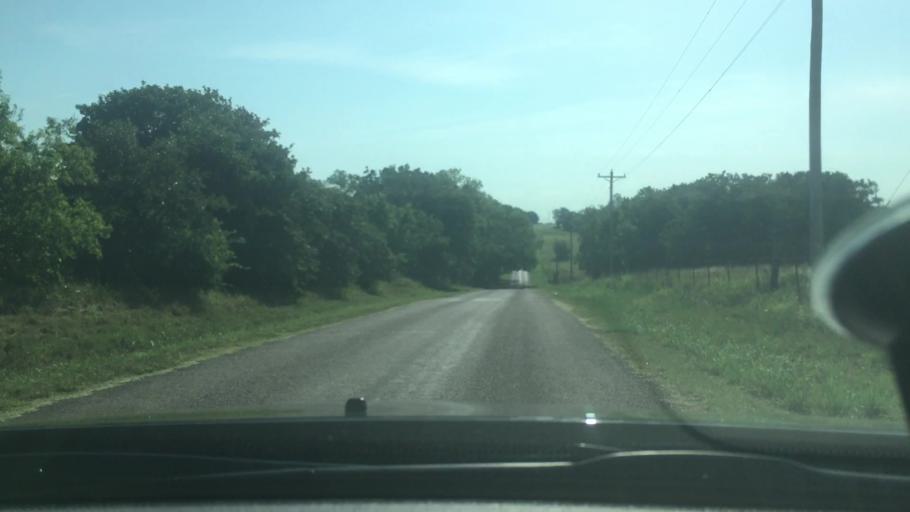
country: US
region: Oklahoma
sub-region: Garvin County
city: Pauls Valley
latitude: 34.6521
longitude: -97.3583
